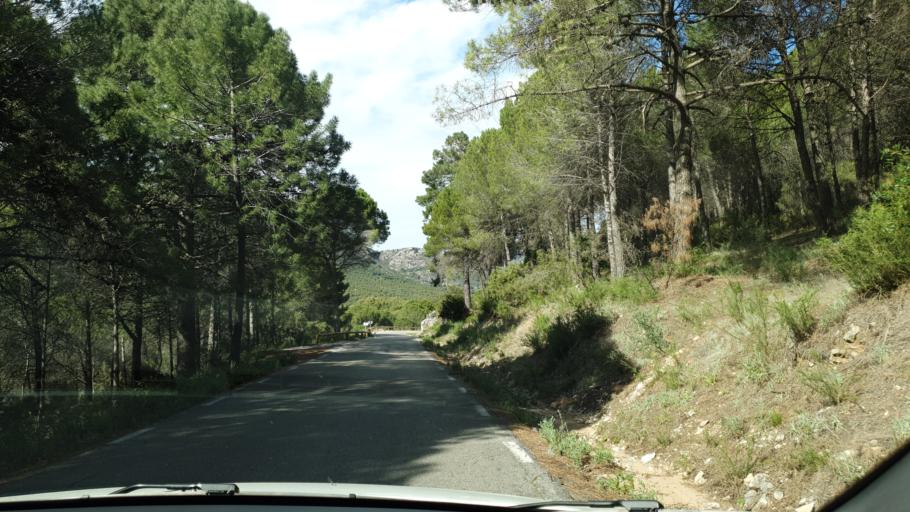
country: ES
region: Andalusia
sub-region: Provincia de Malaga
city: Ojen
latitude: 36.5892
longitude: -4.8580
